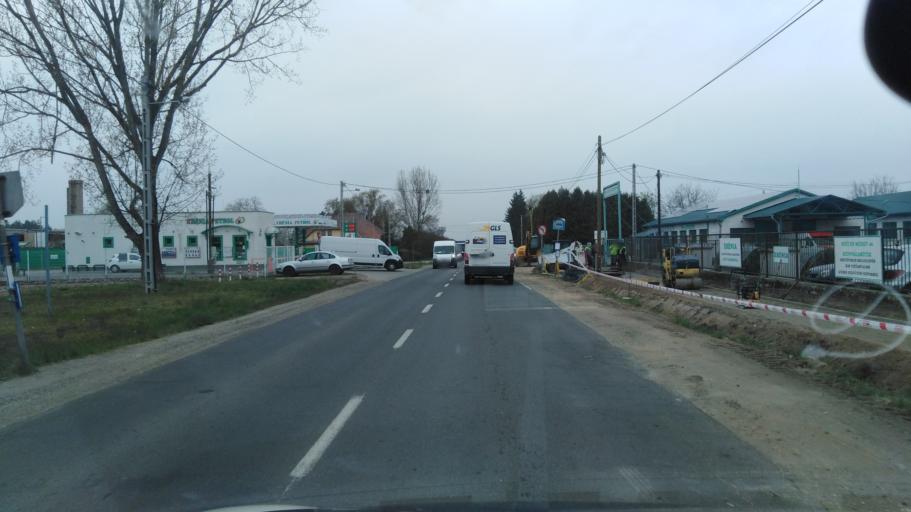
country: HU
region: Nograd
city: Balassagyarmat
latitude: 48.0617
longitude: 19.3041
